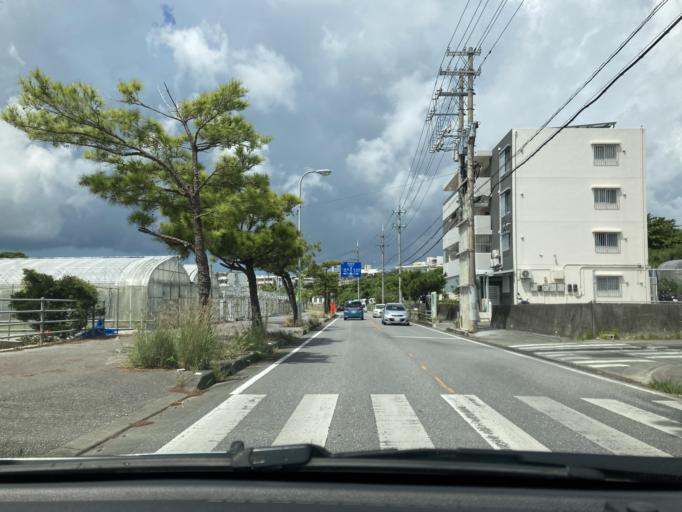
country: JP
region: Okinawa
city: Tomigusuku
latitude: 26.1743
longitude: 127.7515
